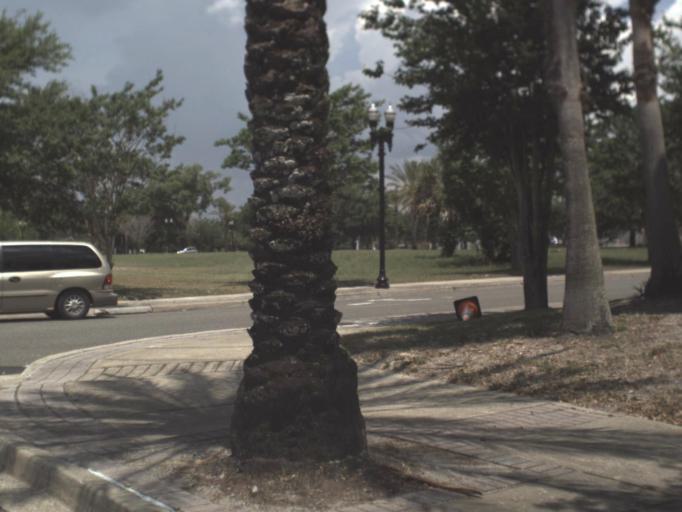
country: US
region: Florida
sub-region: Duval County
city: Jacksonville
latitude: 30.3302
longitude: -81.6683
